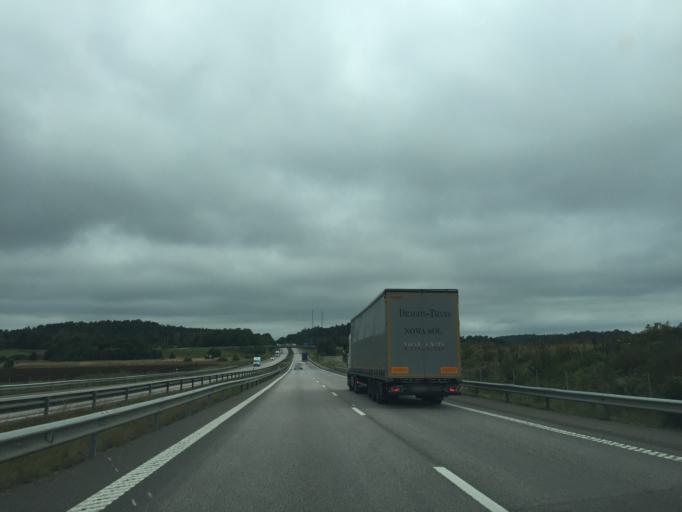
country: SE
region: Halland
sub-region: Kungsbacka Kommun
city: Fjaeras kyrkby
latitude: 57.4147
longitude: 12.1704
